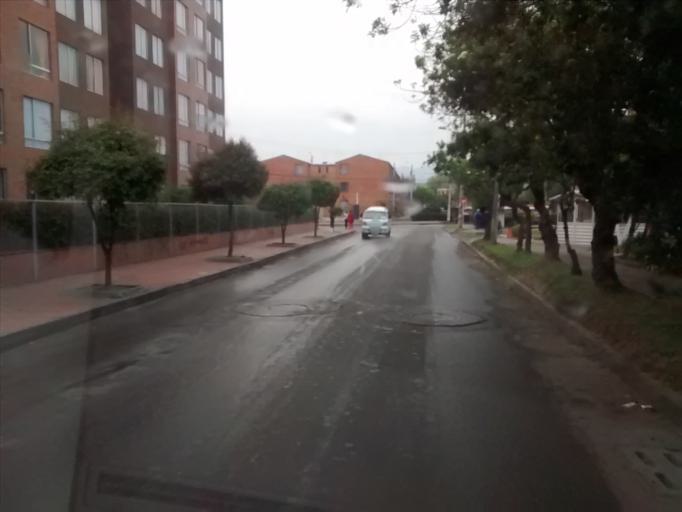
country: CO
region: Cundinamarca
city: Cota
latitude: 4.7573
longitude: -74.1056
